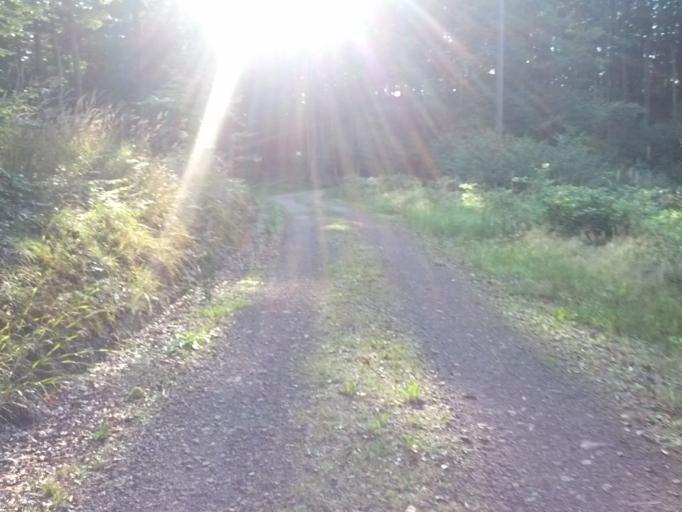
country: DE
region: Thuringia
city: Wolfsburg-Unkeroda
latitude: 50.9377
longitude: 10.3018
